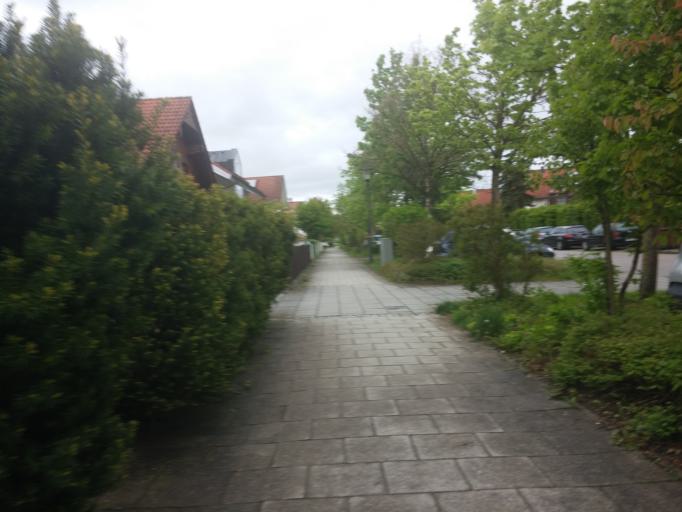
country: DE
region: Bavaria
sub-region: Upper Bavaria
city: Aschheim
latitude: 48.1678
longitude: 11.7107
